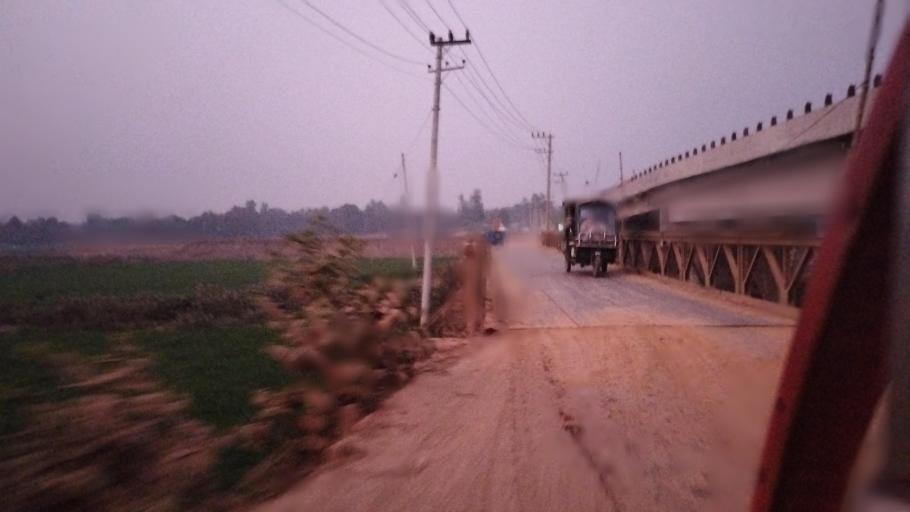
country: BD
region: Dhaka
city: Sakhipur
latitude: 24.3934
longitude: 90.3324
